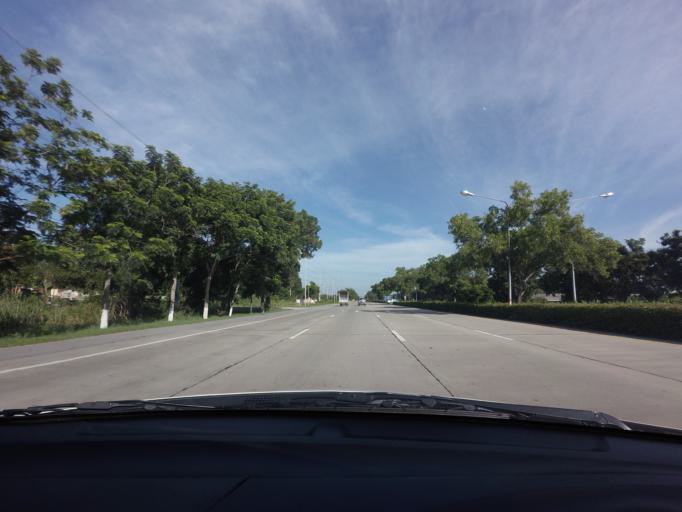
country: TH
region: Suphan Buri
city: Bang Pla Ma
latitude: 14.3918
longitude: 100.1715
